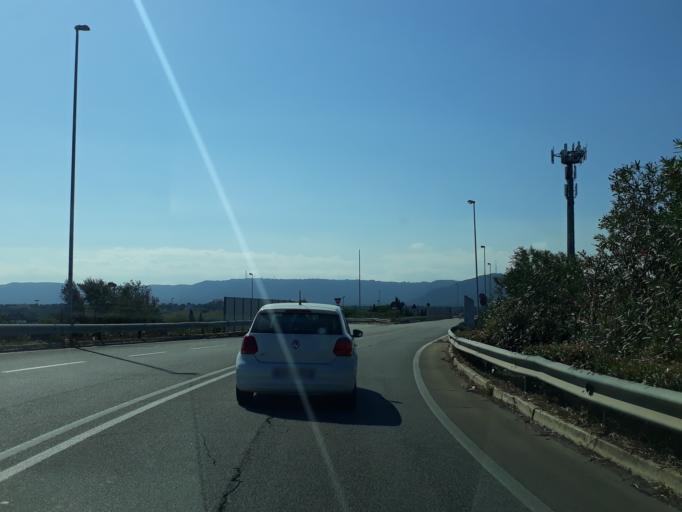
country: IT
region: Apulia
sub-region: Provincia di Bari
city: Monopoli
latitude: 40.9231
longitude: 17.3171
